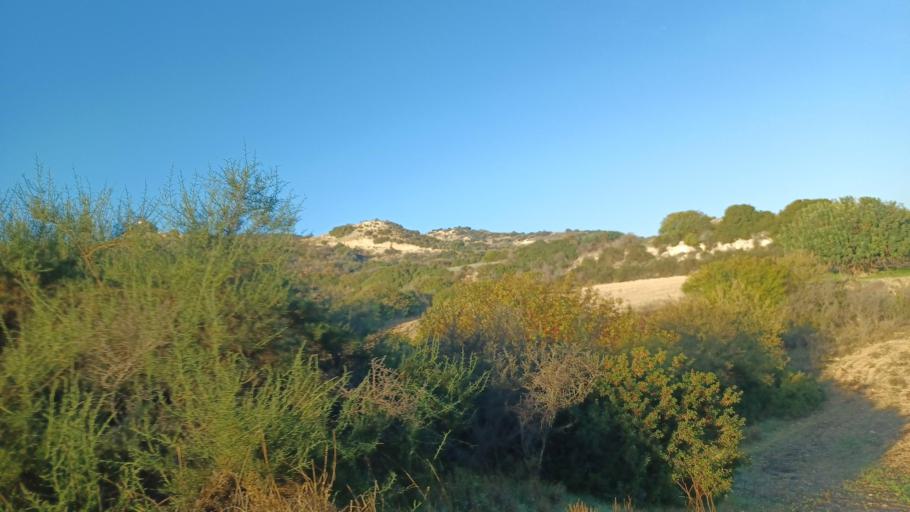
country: CY
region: Pafos
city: Polis
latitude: 35.0017
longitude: 32.4250
